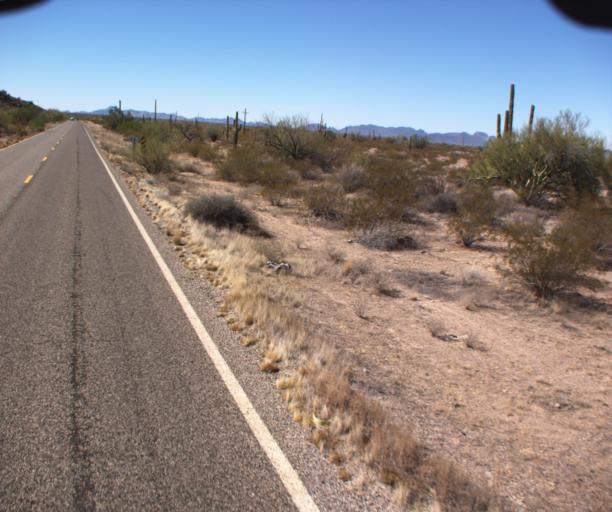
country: US
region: Arizona
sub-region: Pima County
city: Ajo
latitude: 32.2323
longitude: -112.7529
